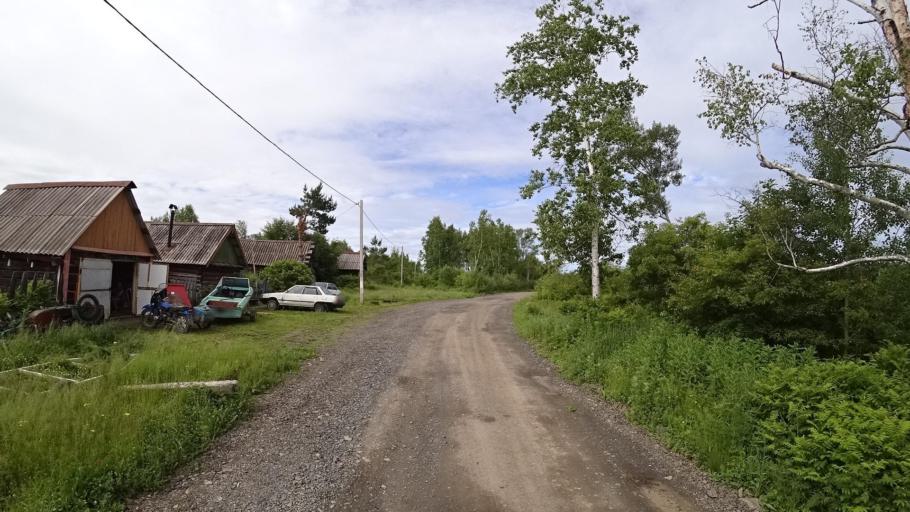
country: RU
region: Khabarovsk Krai
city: Amursk
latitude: 49.8978
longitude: 136.1486
